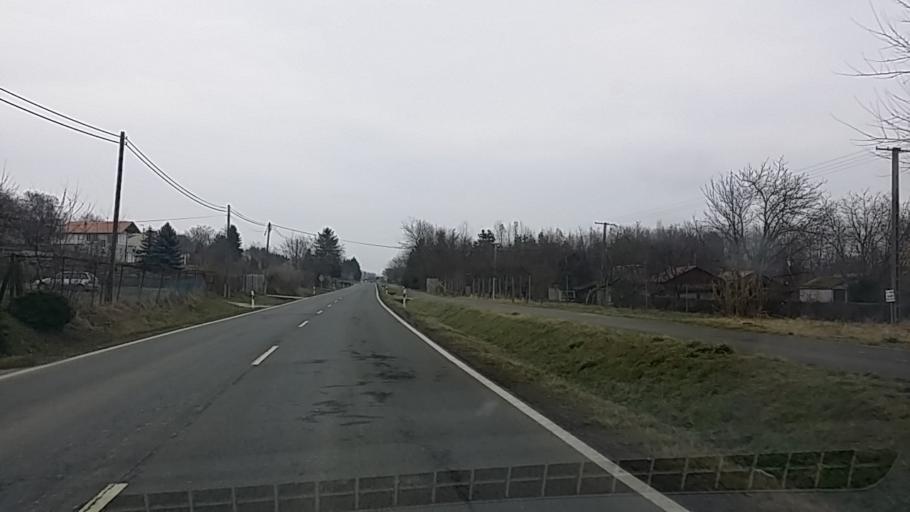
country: HU
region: Baranya
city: Mohacs
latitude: 46.0335
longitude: 18.6887
